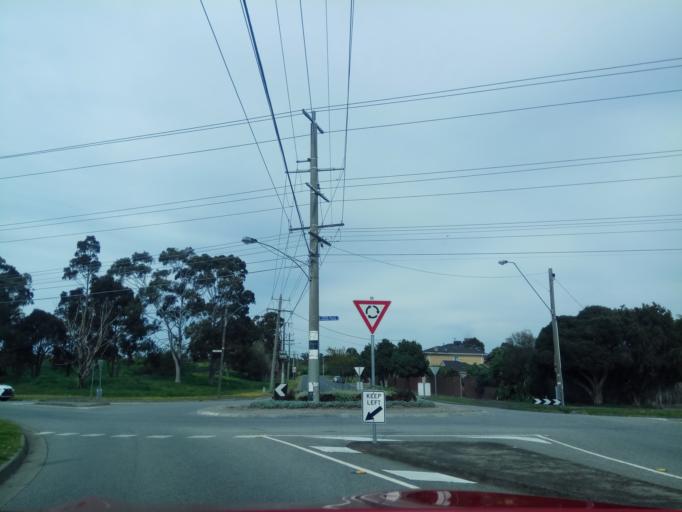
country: AU
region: Victoria
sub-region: Greater Dandenong
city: Springvale South
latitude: -37.9668
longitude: 145.1403
